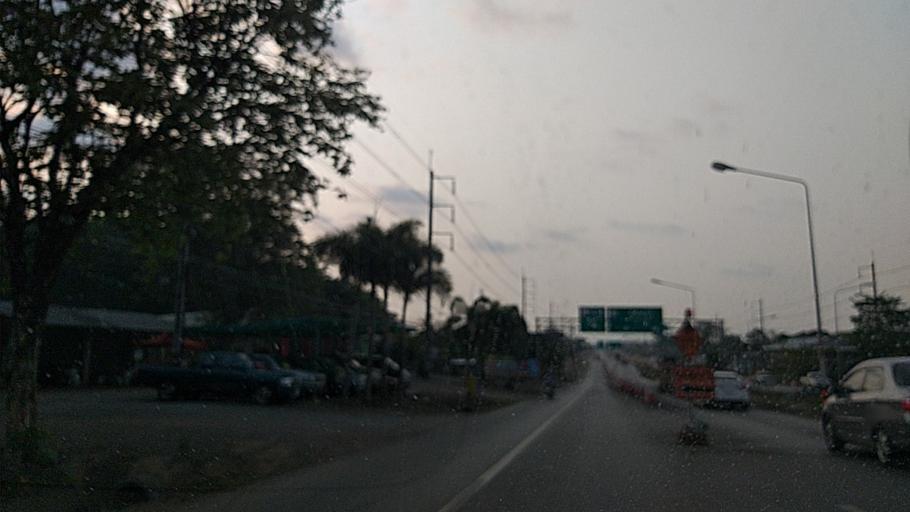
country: TH
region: Trat
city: Khao Saming
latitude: 12.3686
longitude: 102.3921
